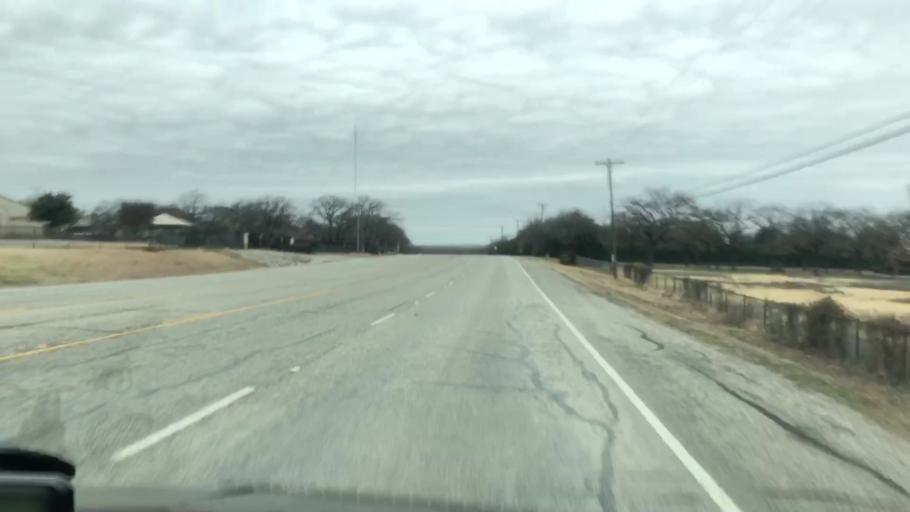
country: US
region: Texas
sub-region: Jack County
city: Jacksboro
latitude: 33.2277
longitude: -98.1755
